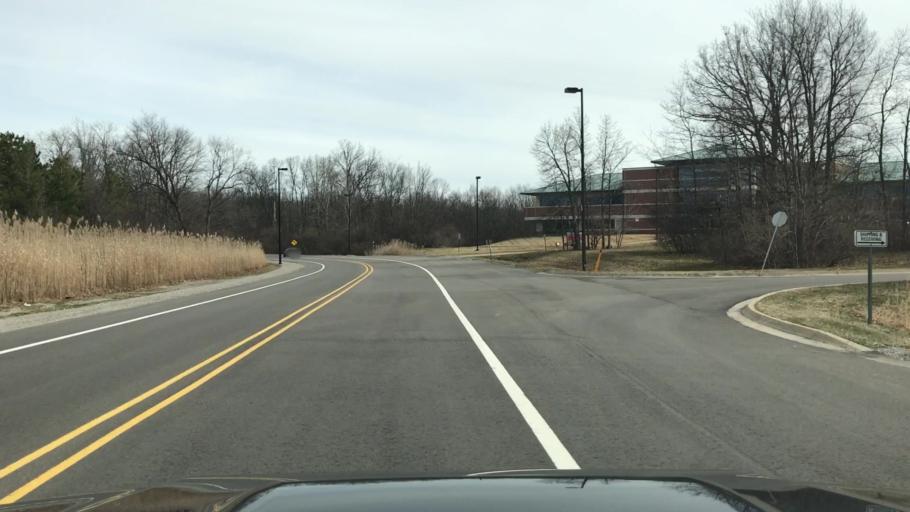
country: US
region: Michigan
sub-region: Washtenaw County
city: Ann Arbor
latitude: 42.2961
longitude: -83.6803
